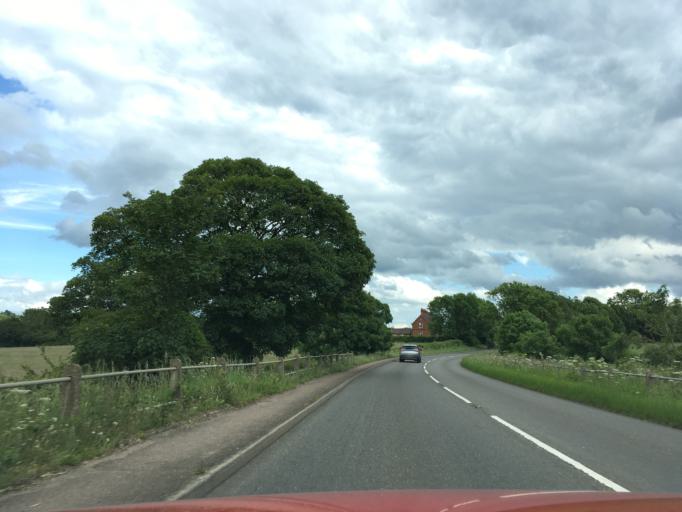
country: GB
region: England
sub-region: Central Bedfordshire
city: Woburn
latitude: 51.9954
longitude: -0.6310
